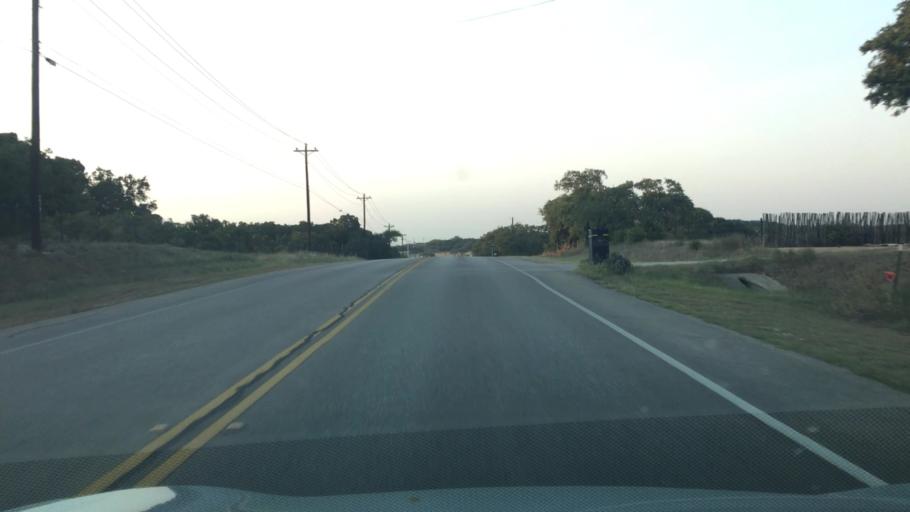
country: US
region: Texas
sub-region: Hays County
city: Dripping Springs
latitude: 30.1591
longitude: -98.0088
